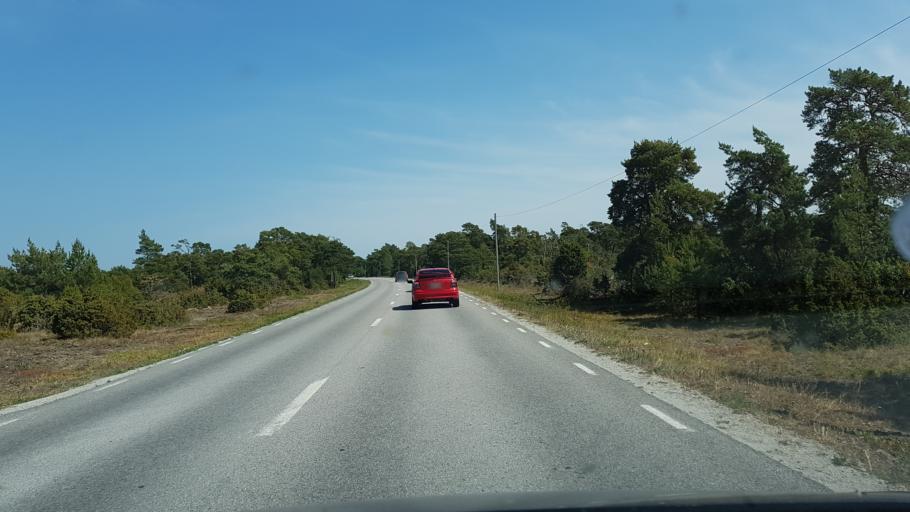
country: SE
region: Gotland
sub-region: Gotland
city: Visby
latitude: 57.6305
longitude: 18.4260
